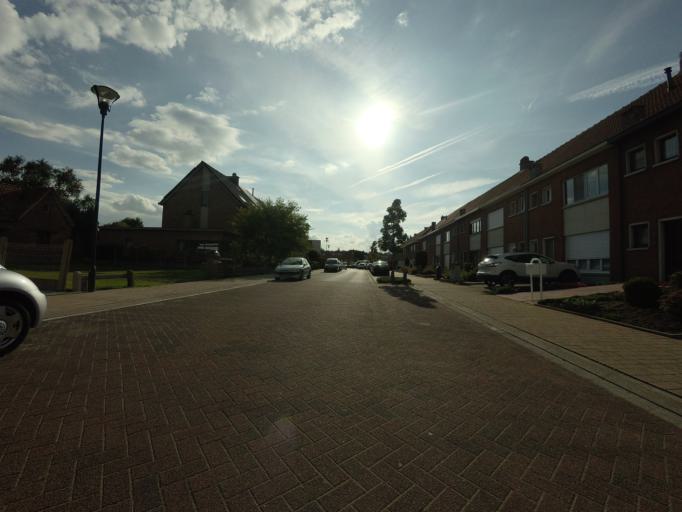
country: BE
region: Flanders
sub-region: Provincie Antwerpen
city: Boom
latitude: 51.1007
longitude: 4.3853
